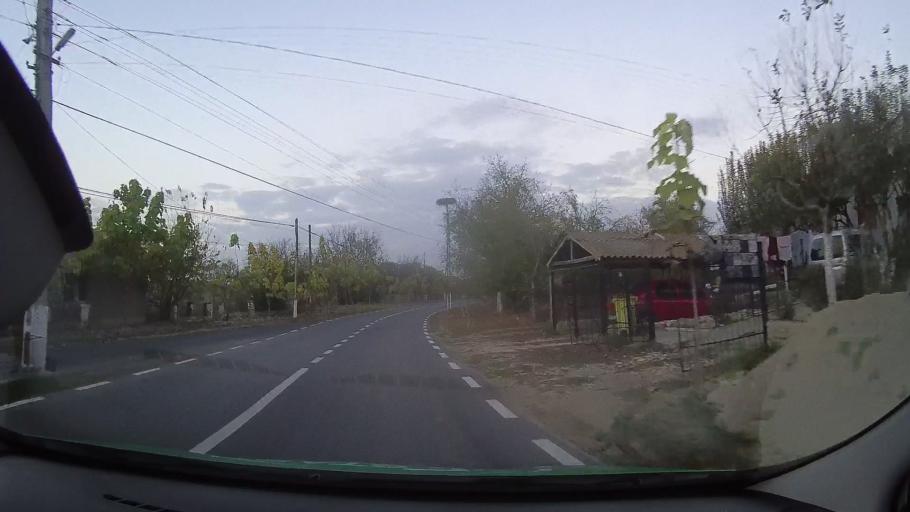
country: RO
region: Constanta
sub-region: Comuna Oltina
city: Oltina
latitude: 44.1698
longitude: 27.6659
